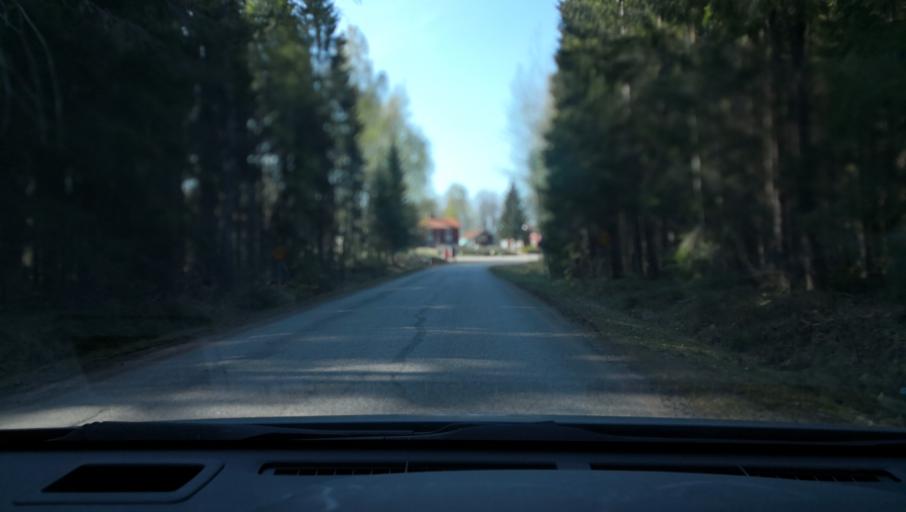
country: SE
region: Uppsala
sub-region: Heby Kommun
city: Tarnsjo
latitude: 60.2822
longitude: 16.8848
